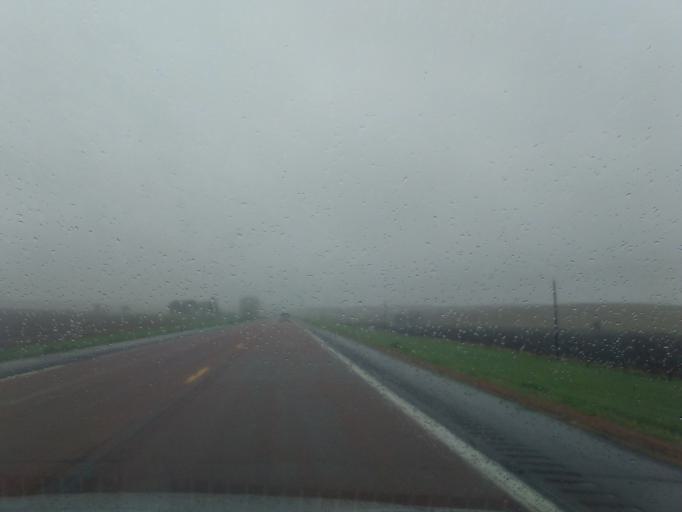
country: US
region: Nebraska
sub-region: Wayne County
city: Wayne
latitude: 42.2357
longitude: -97.1086
